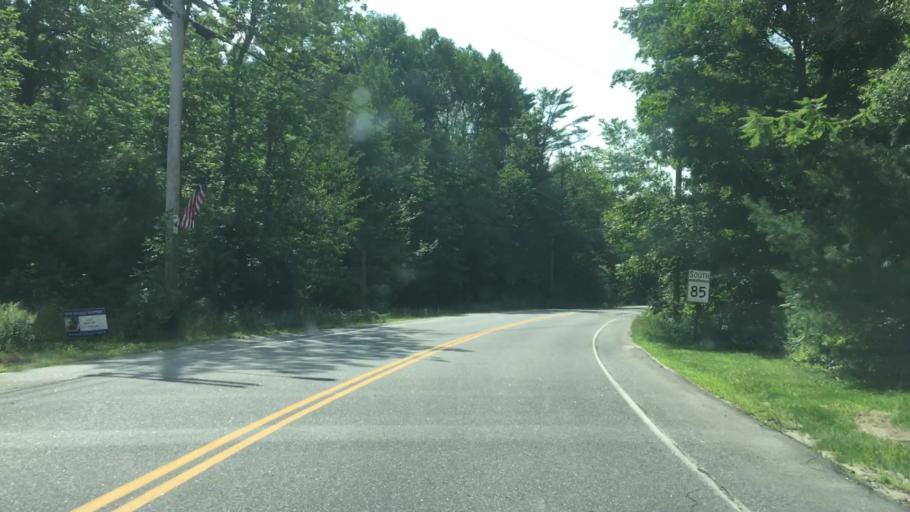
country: US
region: Maine
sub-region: Cumberland County
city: Raymond
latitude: 43.9332
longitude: -70.4391
